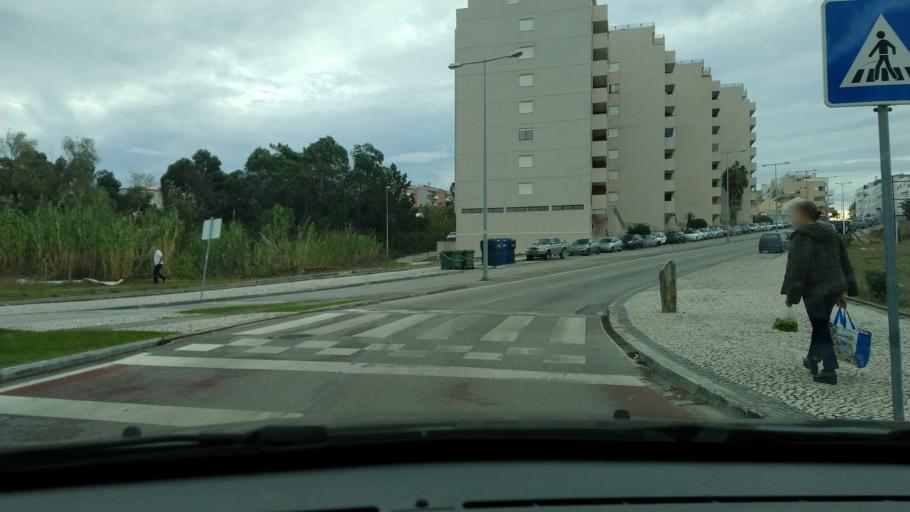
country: PT
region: Coimbra
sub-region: Figueira da Foz
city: Figueira da Foz
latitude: 40.1599
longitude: -8.8582
